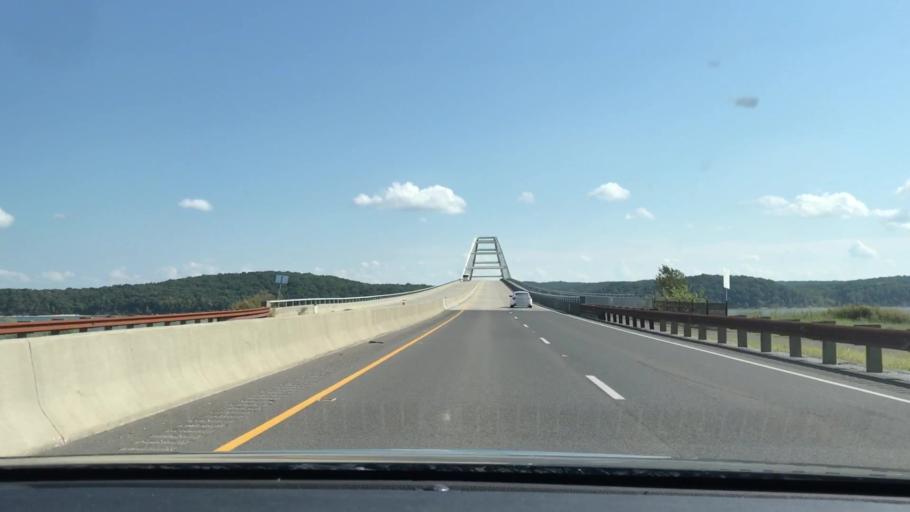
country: US
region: Kentucky
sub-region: Marshall County
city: Benton
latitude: 36.7716
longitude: -88.1270
